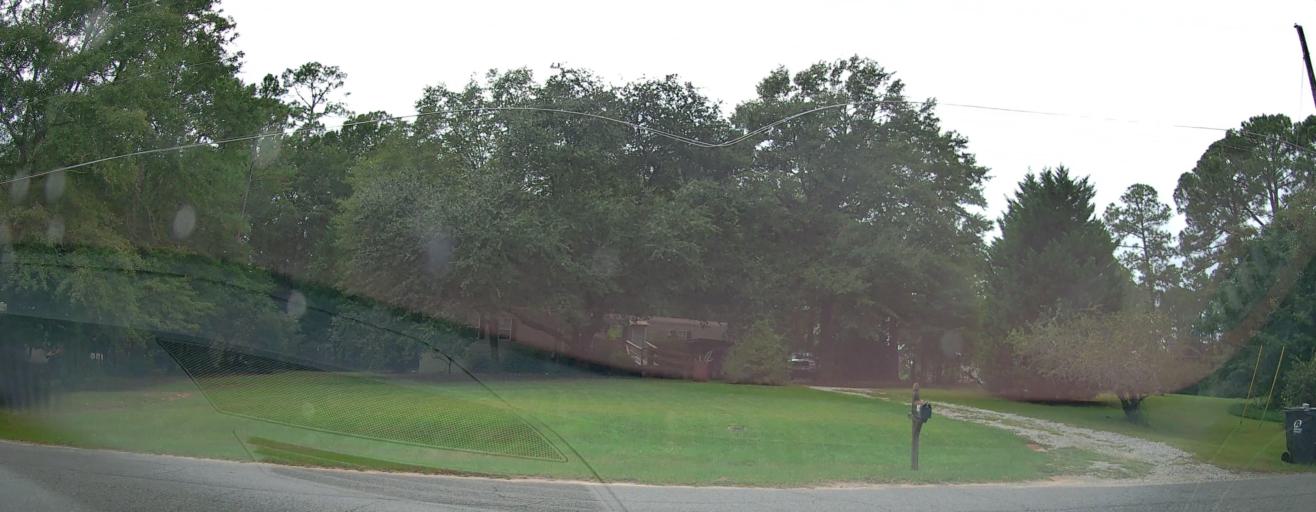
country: US
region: Georgia
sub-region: Peach County
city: Byron
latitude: 32.6753
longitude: -83.7134
